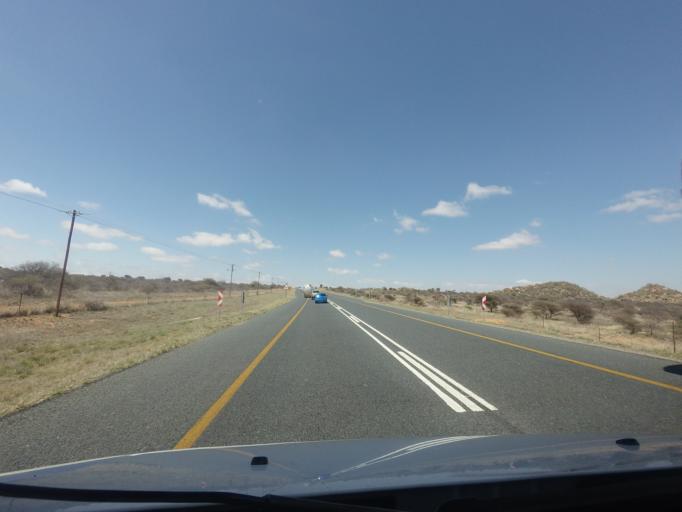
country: ZA
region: Limpopo
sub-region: Vhembe District Municipality
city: Louis Trichardt
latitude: -23.4310
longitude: 29.7478
